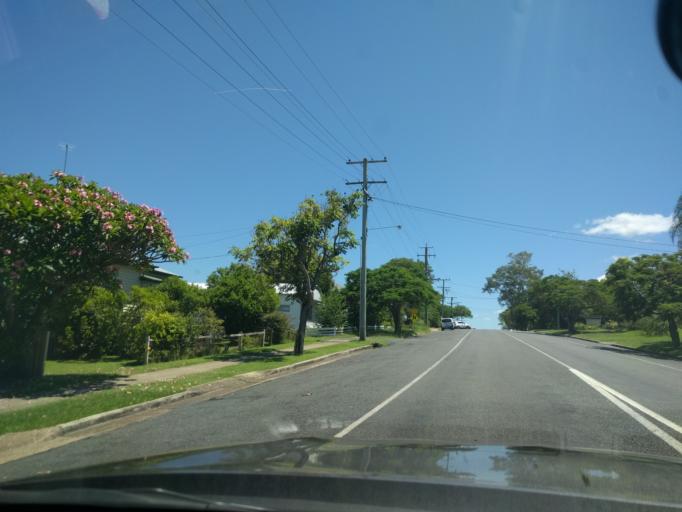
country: AU
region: Queensland
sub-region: Logan
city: Cedar Vale
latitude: -27.9870
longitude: 153.0026
